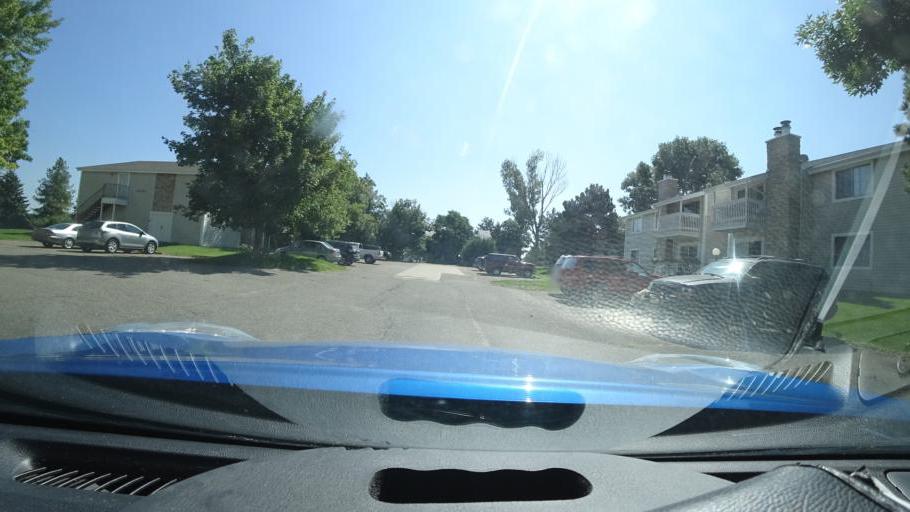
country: US
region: Colorado
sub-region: Adams County
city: Aurora
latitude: 39.6828
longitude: -104.8220
